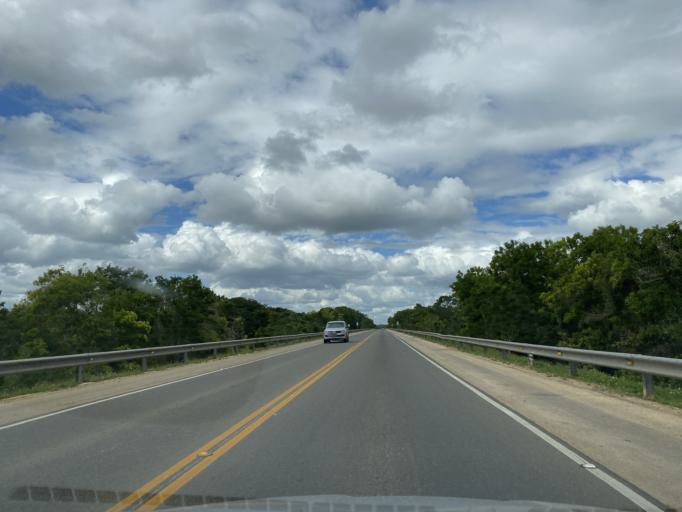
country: DO
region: Santo Domingo
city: Guerra
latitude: 18.5327
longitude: -69.7531
